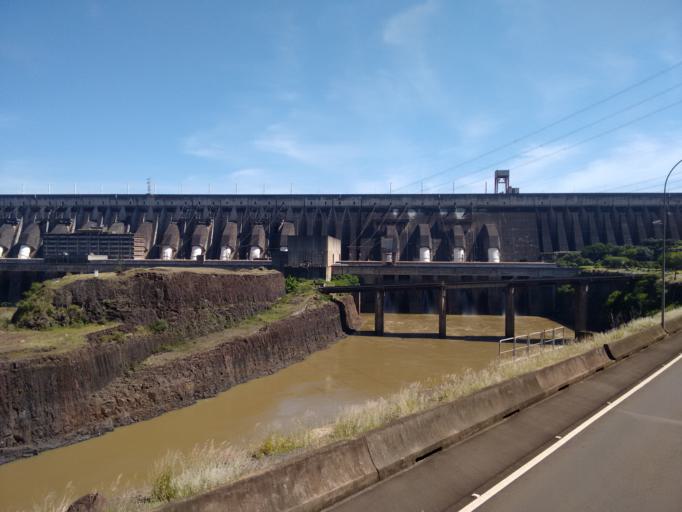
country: PY
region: Alto Parana
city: Ciudad del Este
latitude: -25.4135
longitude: -54.5874
